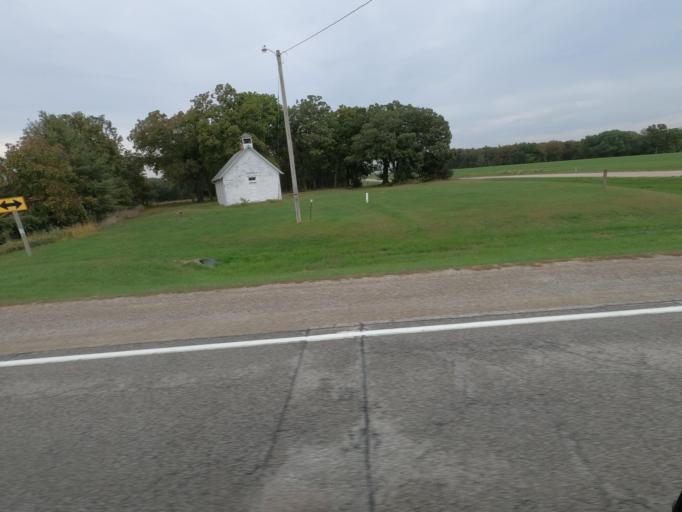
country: US
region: Iowa
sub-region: Van Buren County
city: Keosauqua
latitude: 40.8384
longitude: -92.0062
